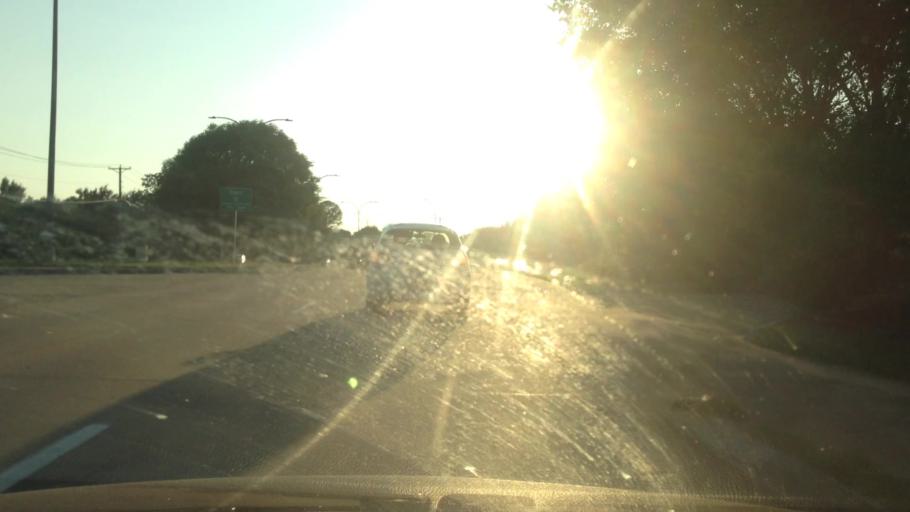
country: US
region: Texas
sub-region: Tarrant County
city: Dalworthington Gardens
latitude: 32.6489
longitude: -97.1494
